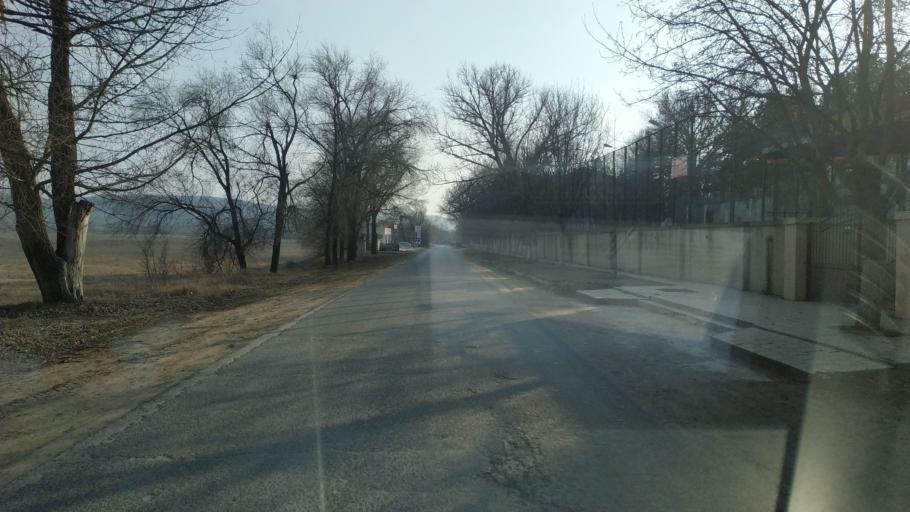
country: MD
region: Hincesti
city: Dancu
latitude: 46.7703
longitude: 28.3463
